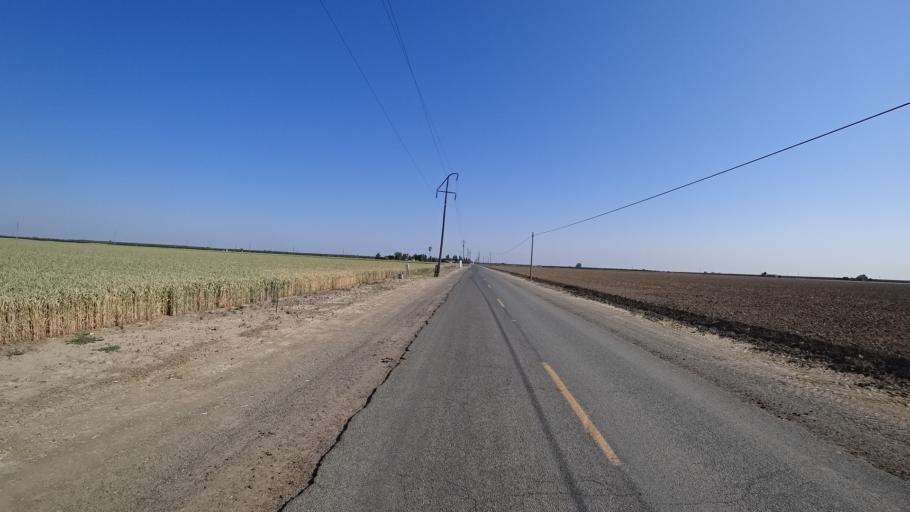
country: US
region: California
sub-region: Kings County
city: Home Garden
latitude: 36.2496
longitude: -119.5831
